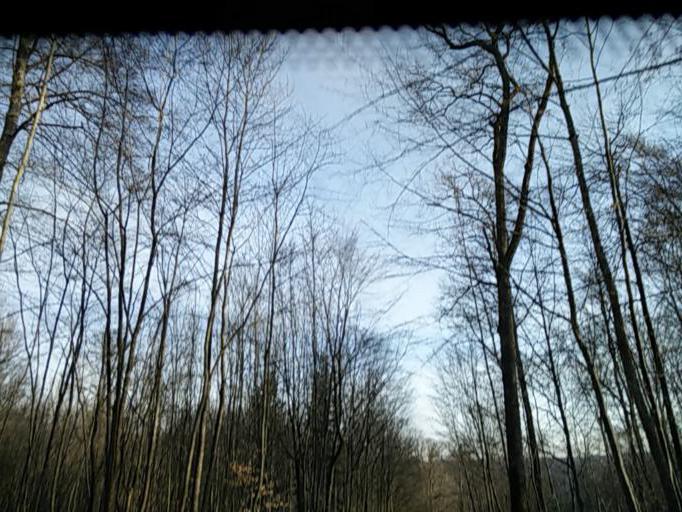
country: DE
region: Baden-Wuerttemberg
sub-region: Tuebingen Region
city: Tuebingen
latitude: 48.5550
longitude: 9.0562
